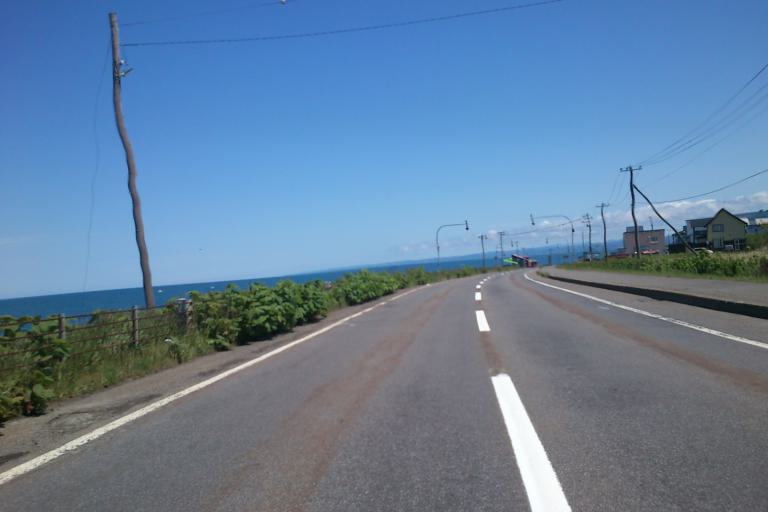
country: JP
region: Hokkaido
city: Rumoi
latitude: 43.8511
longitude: 141.5069
